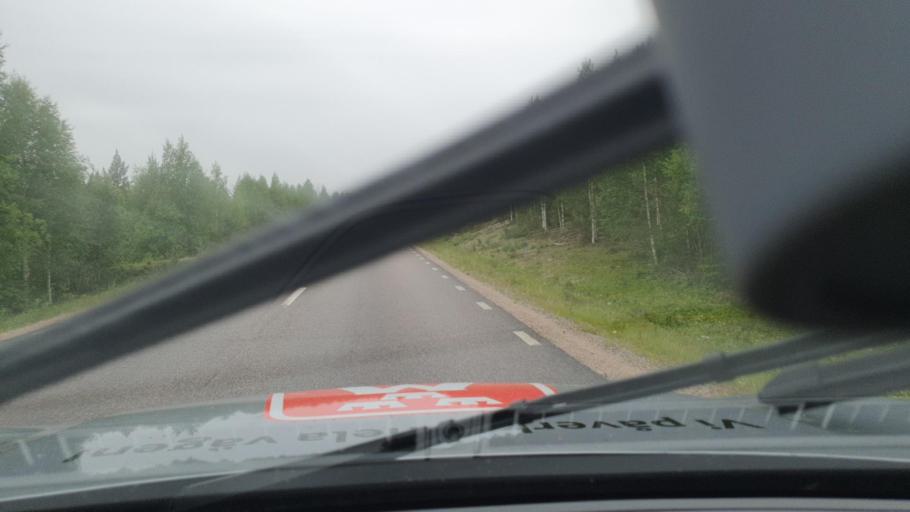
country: SE
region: Norrbotten
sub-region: Overtornea Kommun
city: OEvertornea
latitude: 66.4030
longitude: 23.4879
